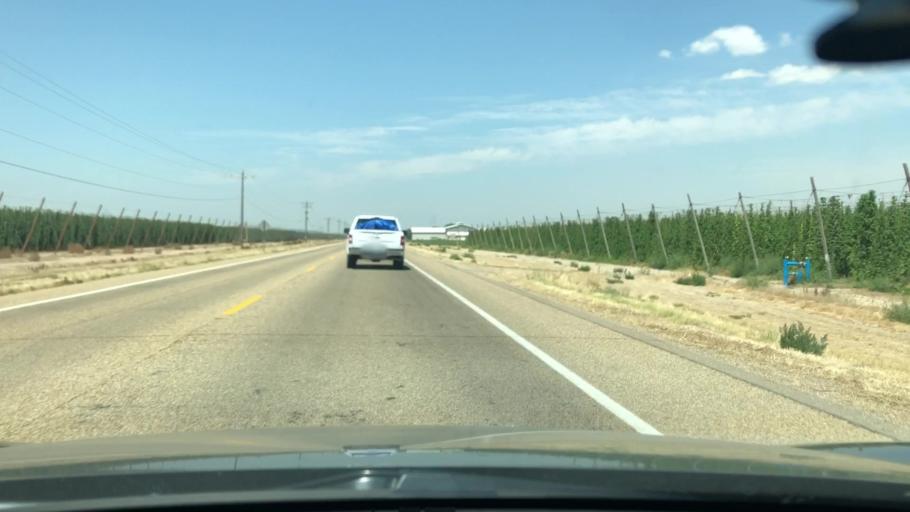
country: US
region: Idaho
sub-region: Canyon County
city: Wilder
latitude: 43.6995
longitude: -116.9120
